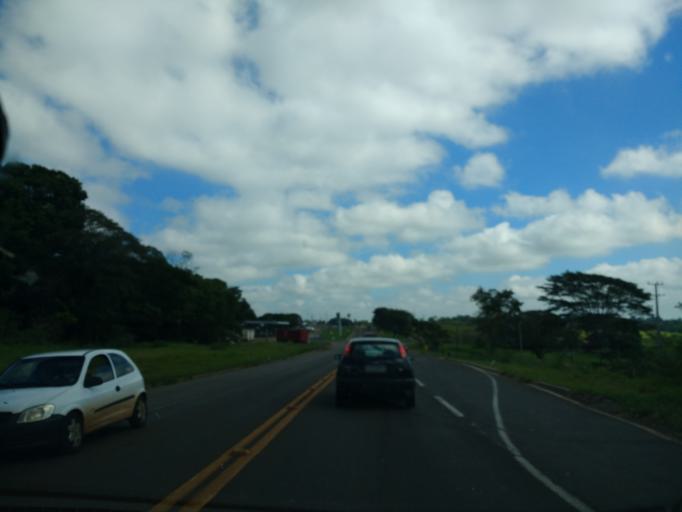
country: BR
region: Parana
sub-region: Cruzeiro Do Oeste
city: Cruzeiro do Oeste
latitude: -23.7650
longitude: -53.1254
